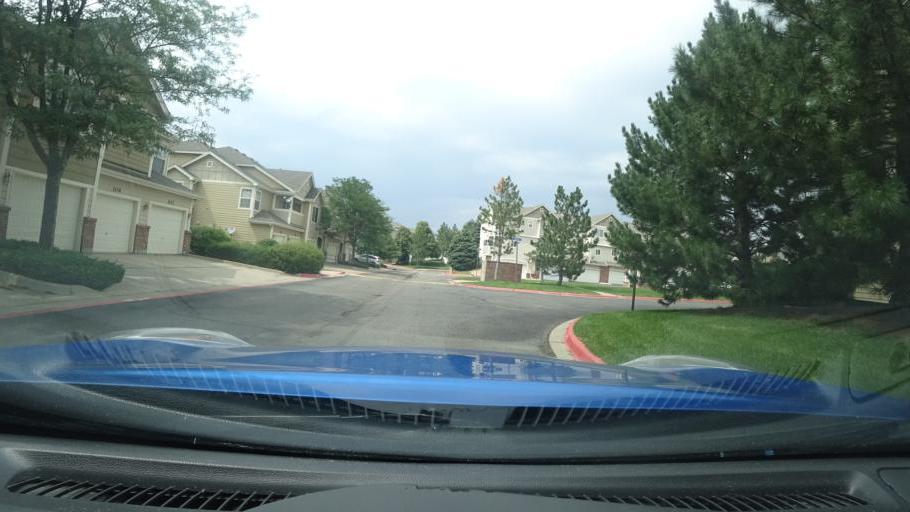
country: US
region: Colorado
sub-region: Adams County
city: Aurora
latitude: 39.6899
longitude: -104.7644
